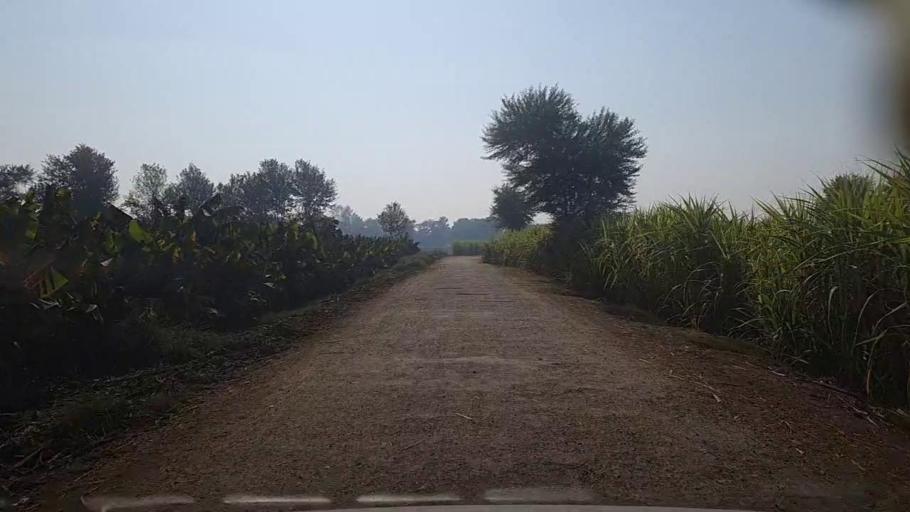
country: PK
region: Sindh
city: Kandiari
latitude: 26.9935
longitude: 68.4704
